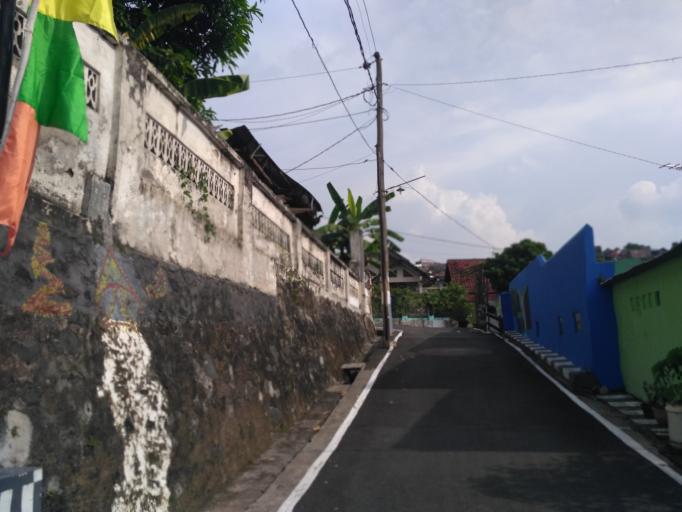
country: ID
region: Central Java
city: Semarang
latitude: -7.0130
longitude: 110.4435
